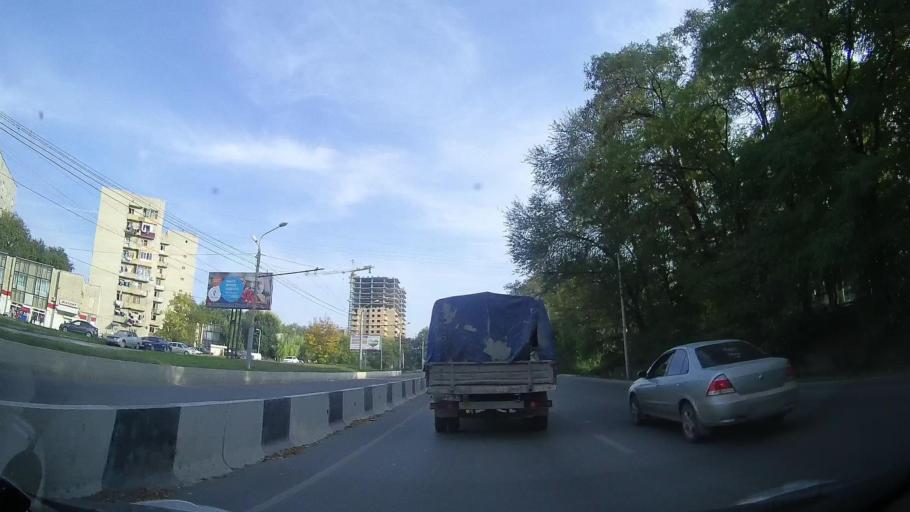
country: RU
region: Rostov
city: Temernik
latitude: 47.2888
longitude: 39.7403
